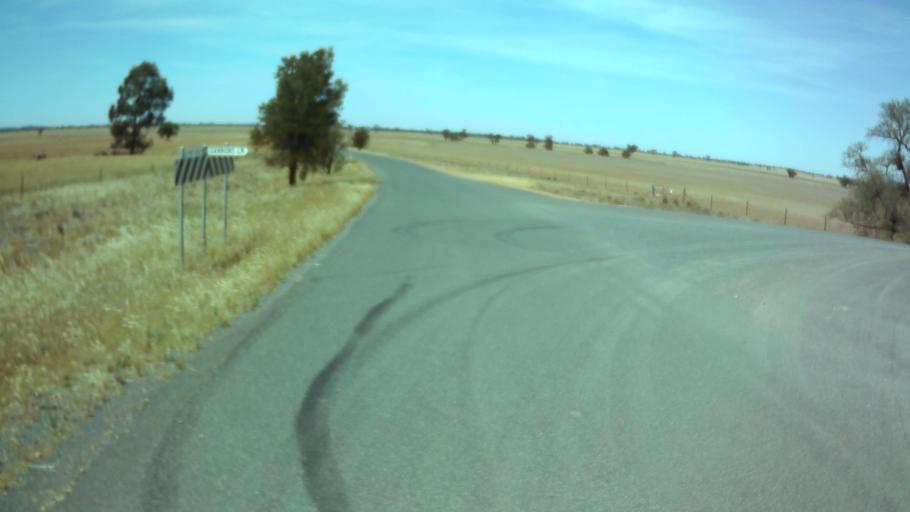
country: AU
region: New South Wales
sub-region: Weddin
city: Grenfell
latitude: -33.8591
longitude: 147.9290
